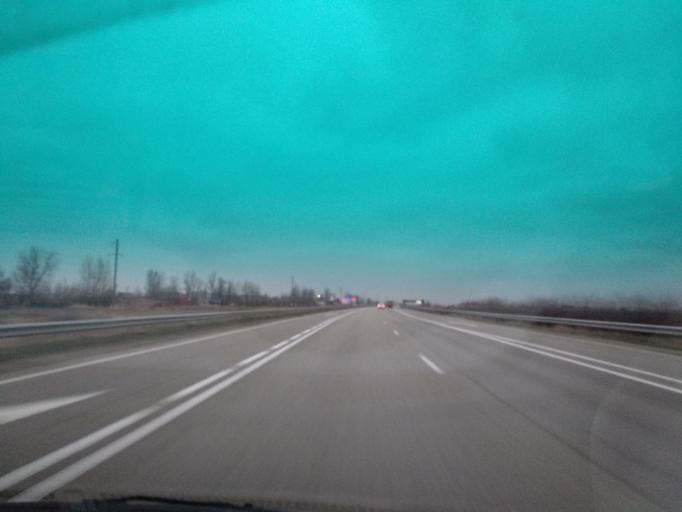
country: RU
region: Adygeya
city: Adygeysk
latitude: 44.8882
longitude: 39.1713
